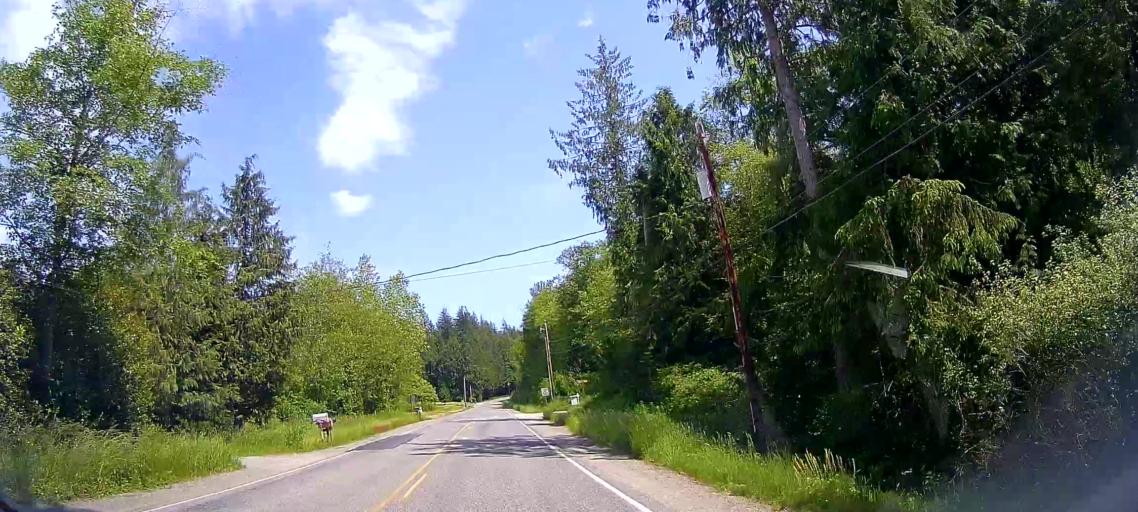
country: US
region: Washington
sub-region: Skagit County
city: Big Lake
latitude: 48.3947
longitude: -122.2762
